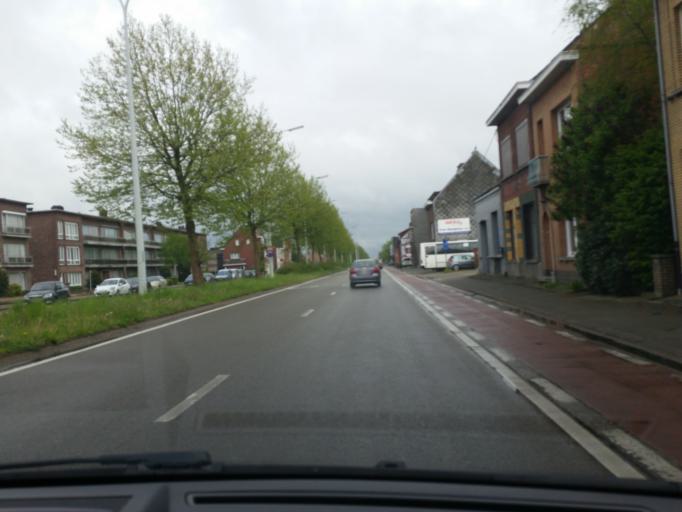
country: BE
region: Flanders
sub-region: Provincie Antwerpen
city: Boechout
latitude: 51.1593
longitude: 4.5113
